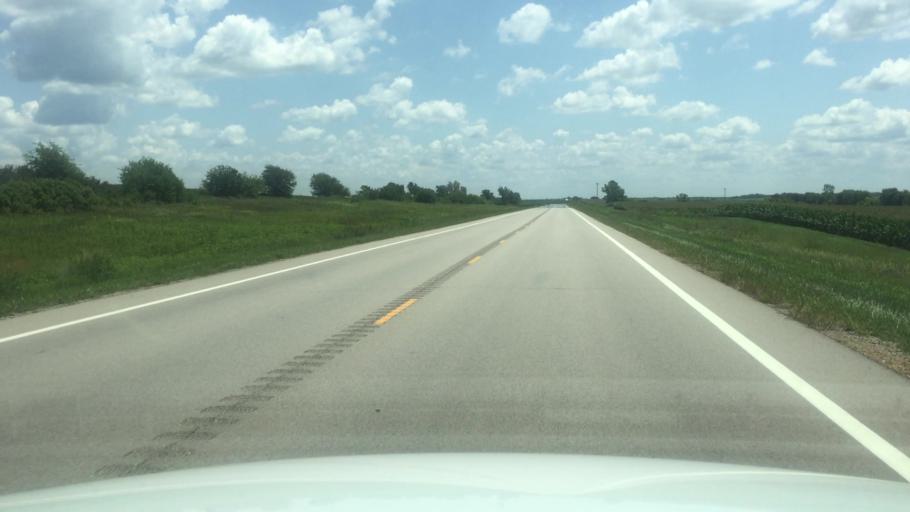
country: US
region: Kansas
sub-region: Brown County
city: Horton
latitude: 39.5988
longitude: -95.3356
